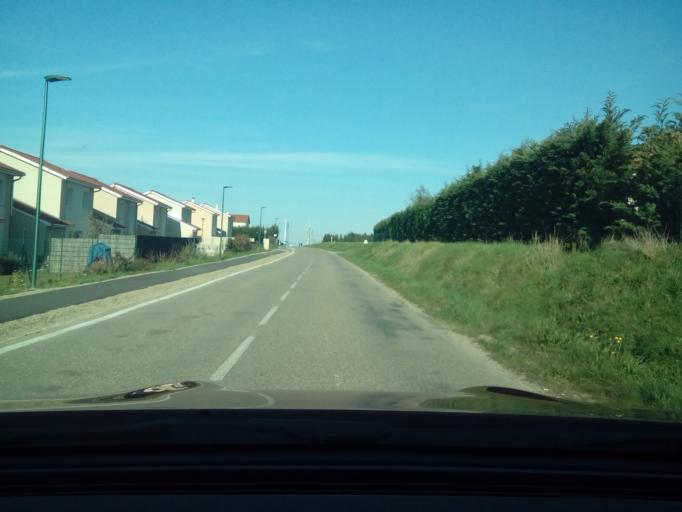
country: FR
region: Rhone-Alpes
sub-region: Departement de l'Isere
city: Serpaize
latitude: 45.5591
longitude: 4.9212
